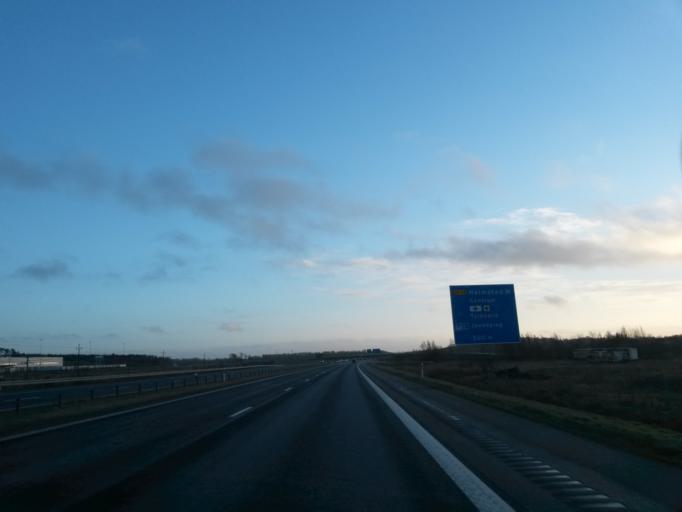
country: SE
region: Halland
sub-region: Halmstads Kommun
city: Halmstad
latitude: 56.7211
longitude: 12.8846
